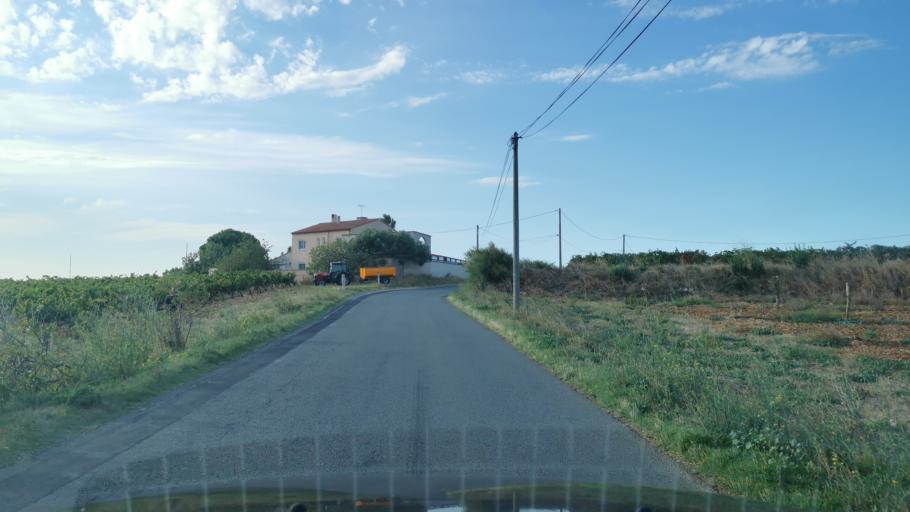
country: FR
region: Languedoc-Roussillon
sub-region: Departement de l'Aude
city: Narbonne
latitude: 43.1533
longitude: 3.0158
